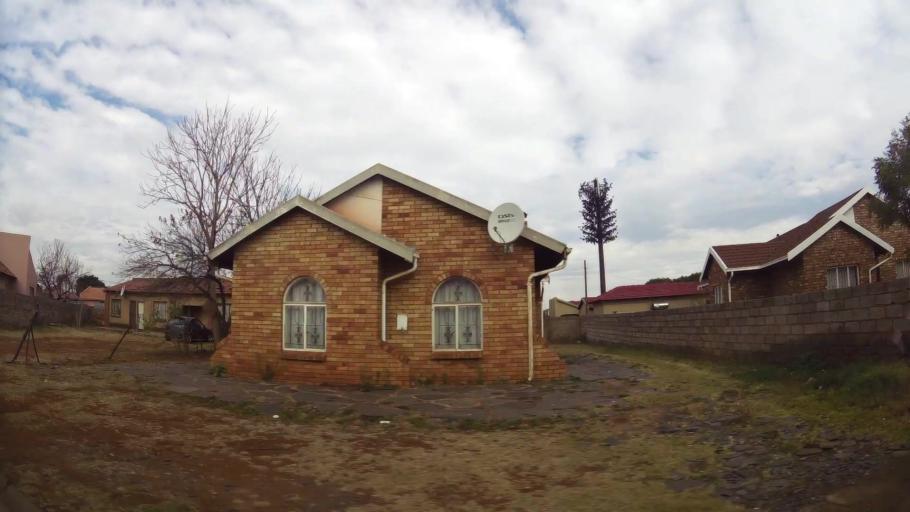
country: ZA
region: Gauteng
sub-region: Ekurhuleni Metropolitan Municipality
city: Germiston
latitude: -26.3238
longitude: 28.1808
